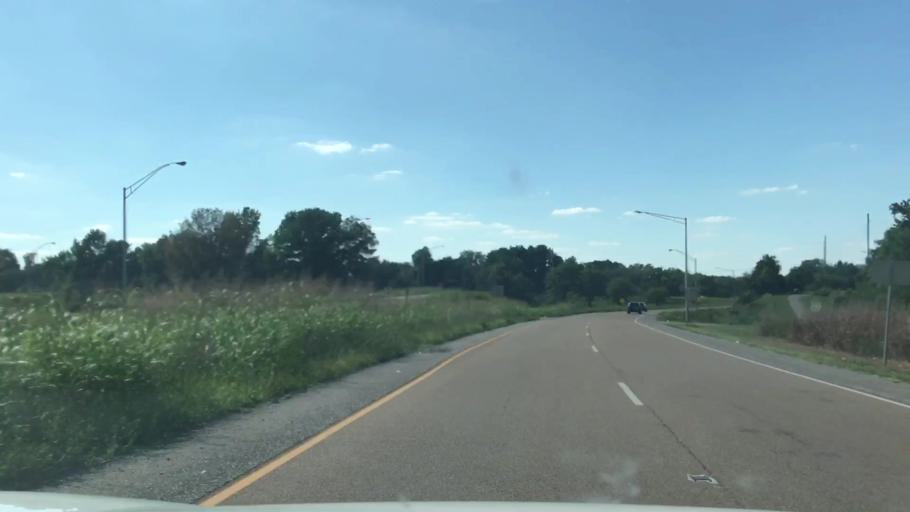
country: US
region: Illinois
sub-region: Saint Clair County
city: Alorton
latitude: 38.5479
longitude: -90.0637
